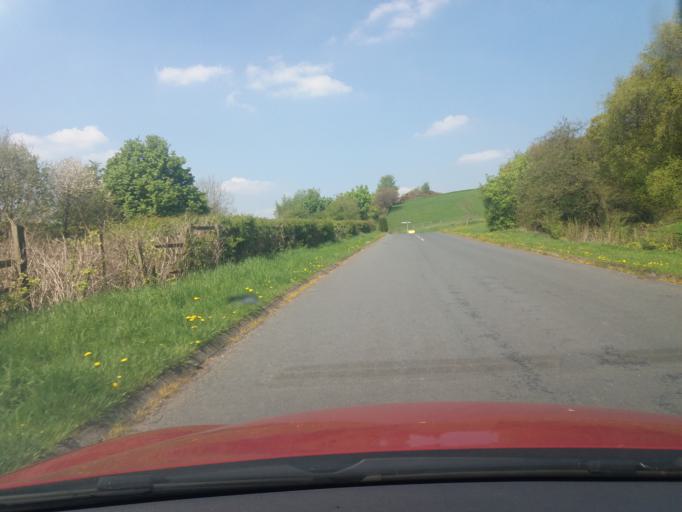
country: GB
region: England
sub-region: Lancashire
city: Clayton-le-Woods
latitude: 53.6942
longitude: -2.6249
